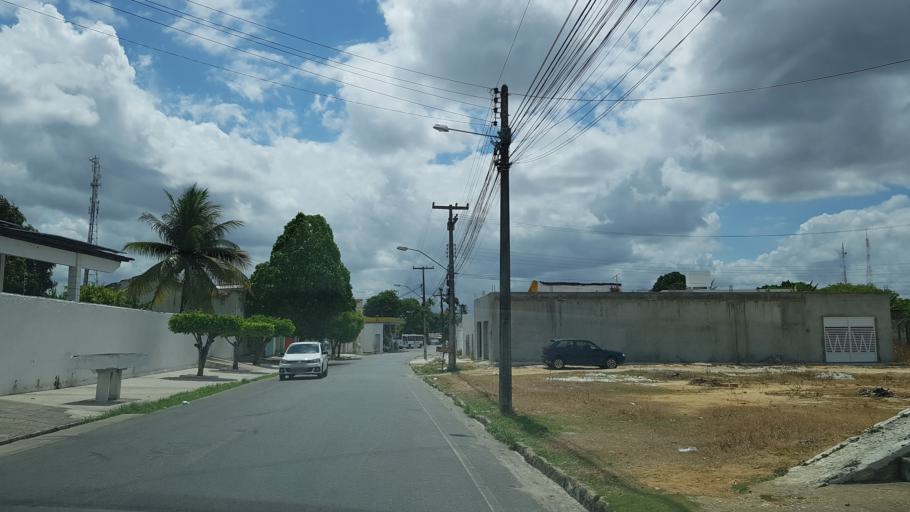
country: BR
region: Alagoas
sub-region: Penedo
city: Penedo
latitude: -10.2822
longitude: -36.5686
